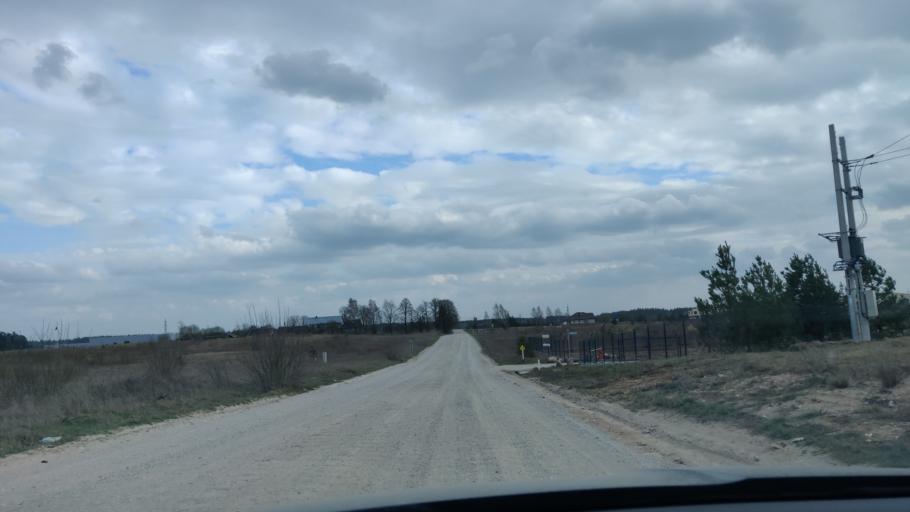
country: LT
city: Lentvaris
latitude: 54.6188
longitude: 25.0666
